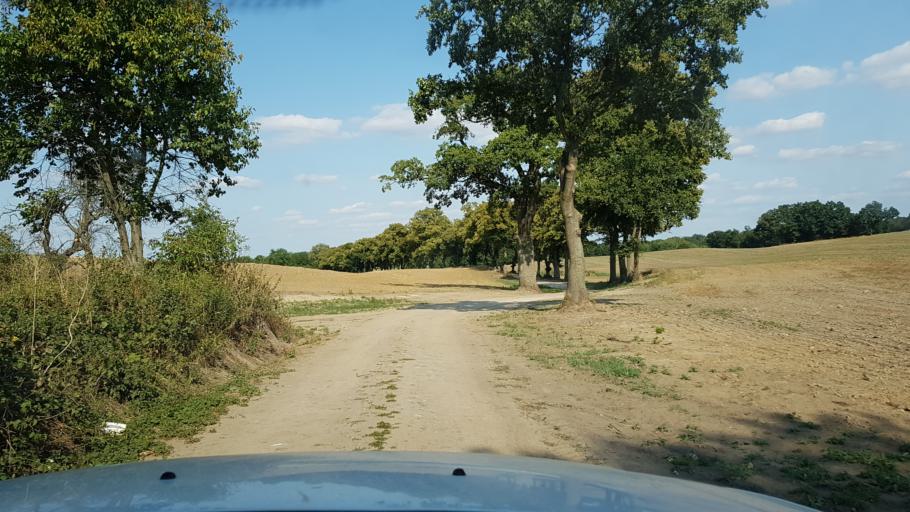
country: PL
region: West Pomeranian Voivodeship
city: Trzcinsko Zdroj
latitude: 52.9050
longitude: 14.5777
